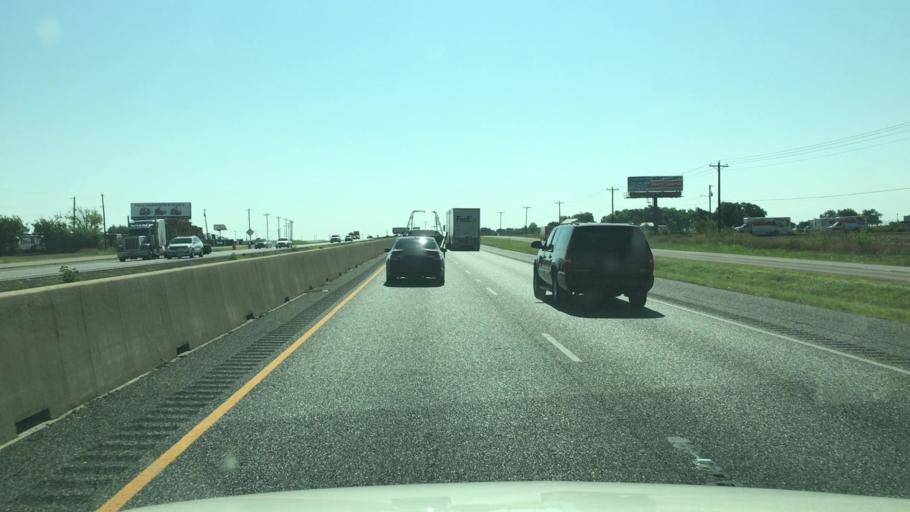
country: US
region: Texas
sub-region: Rockwall County
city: Royse City
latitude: 32.9809
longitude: -96.2829
